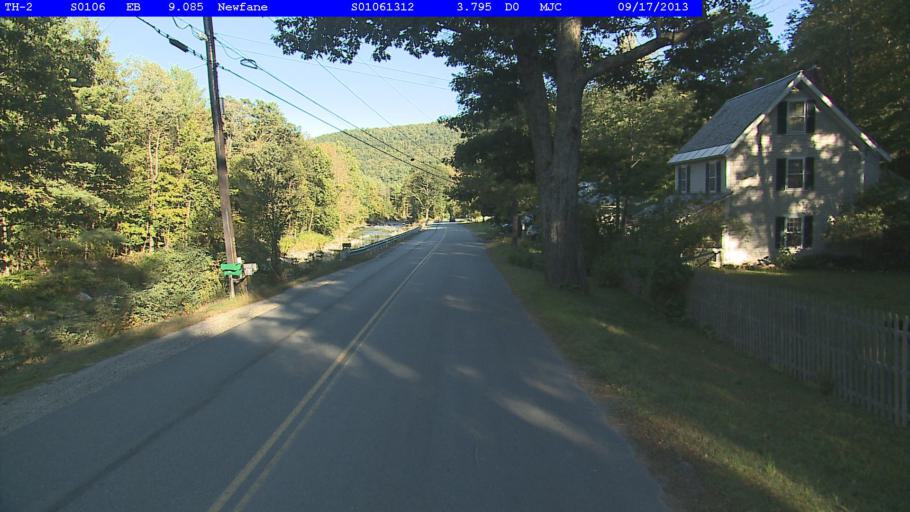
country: US
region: Vermont
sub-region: Windham County
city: Newfane
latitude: 42.9372
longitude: -72.7040
